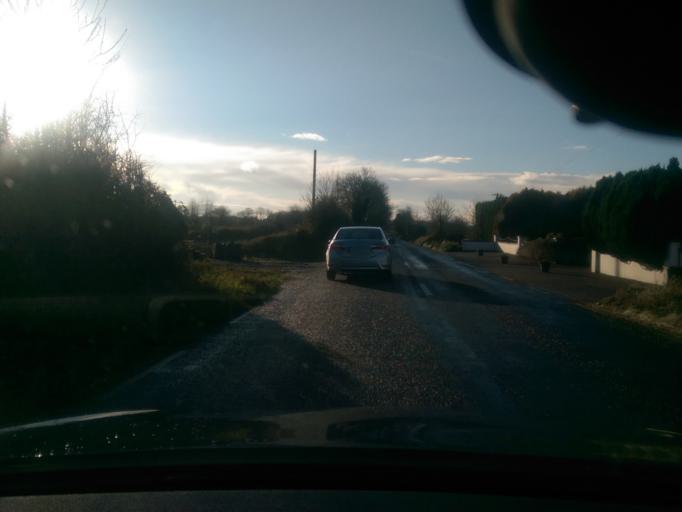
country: IE
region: Connaught
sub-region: County Galway
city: Athenry
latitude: 53.4051
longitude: -8.6393
